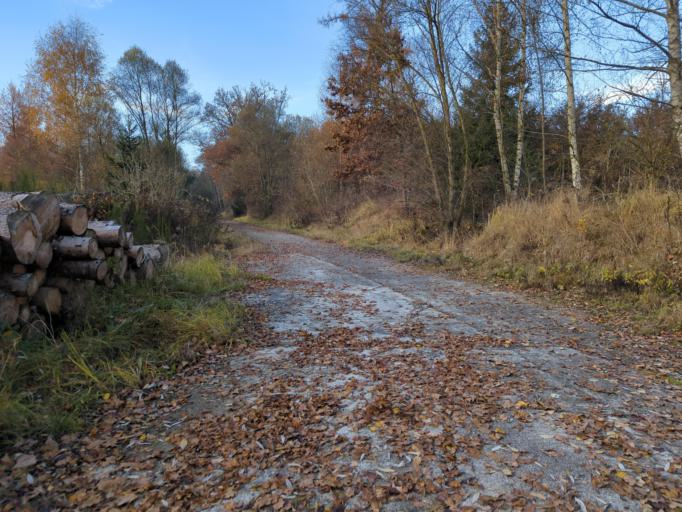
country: DE
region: Bavaria
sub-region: Swabia
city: Rettenbach
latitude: 48.4246
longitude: 10.3208
